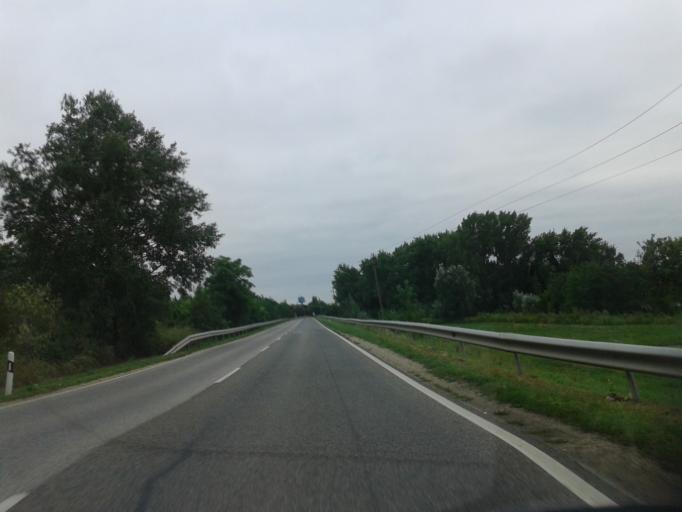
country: HU
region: Pest
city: Domsod
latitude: 47.1051
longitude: 19.0125
